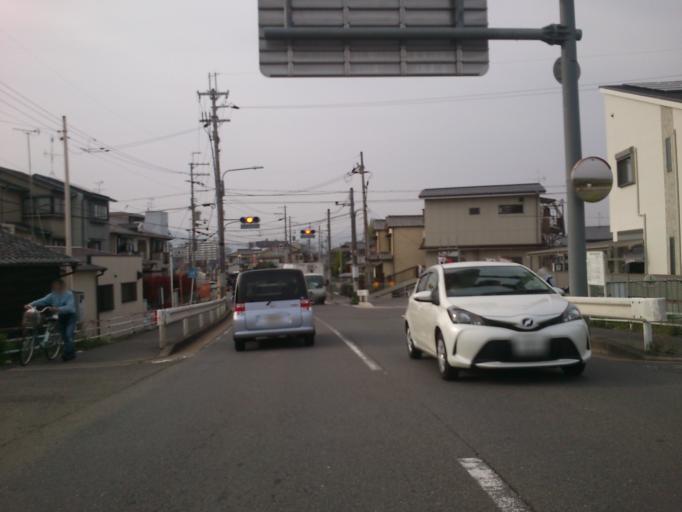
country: JP
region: Kyoto
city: Yawata
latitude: 34.8975
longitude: 135.7181
